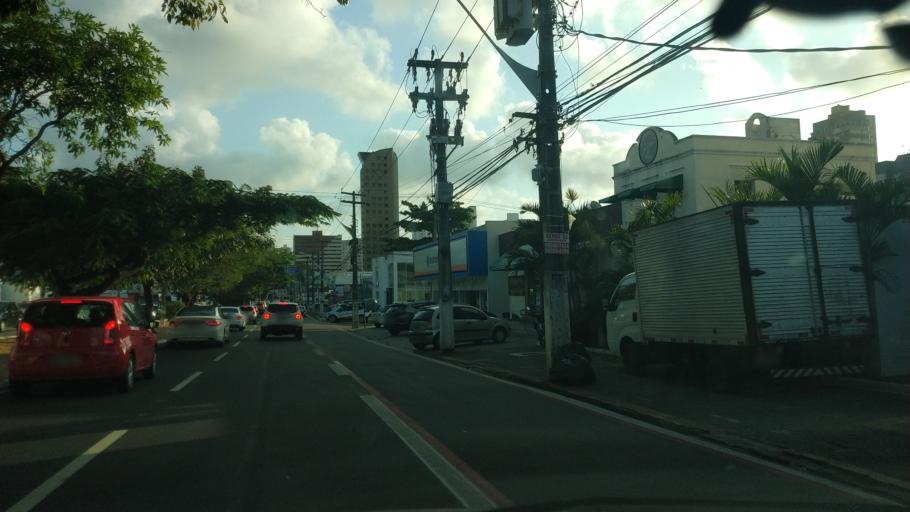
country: BR
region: Rio Grande do Norte
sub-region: Natal
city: Natal
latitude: -5.7951
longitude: -35.1987
